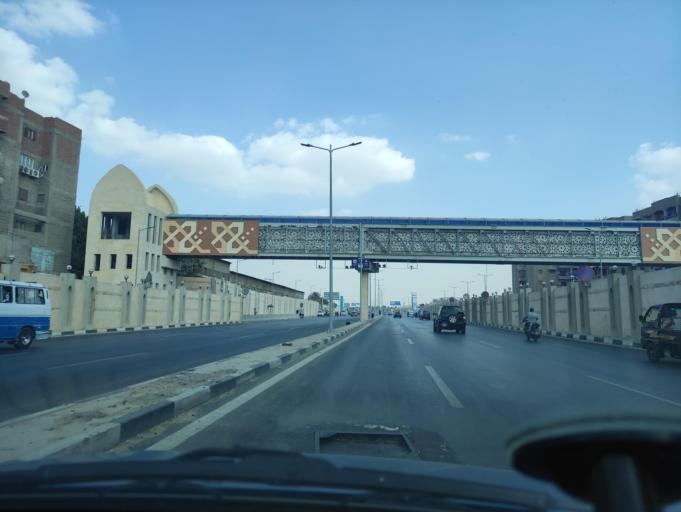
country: EG
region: Muhafazat al Qahirah
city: Cairo
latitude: 30.0434
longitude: 31.2951
